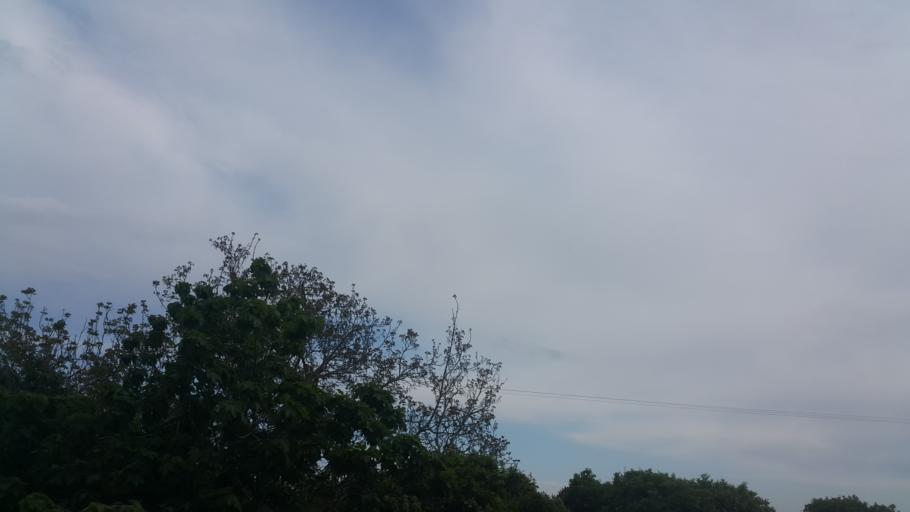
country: TR
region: Mersin
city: Yenice
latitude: 36.9694
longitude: 35.0482
